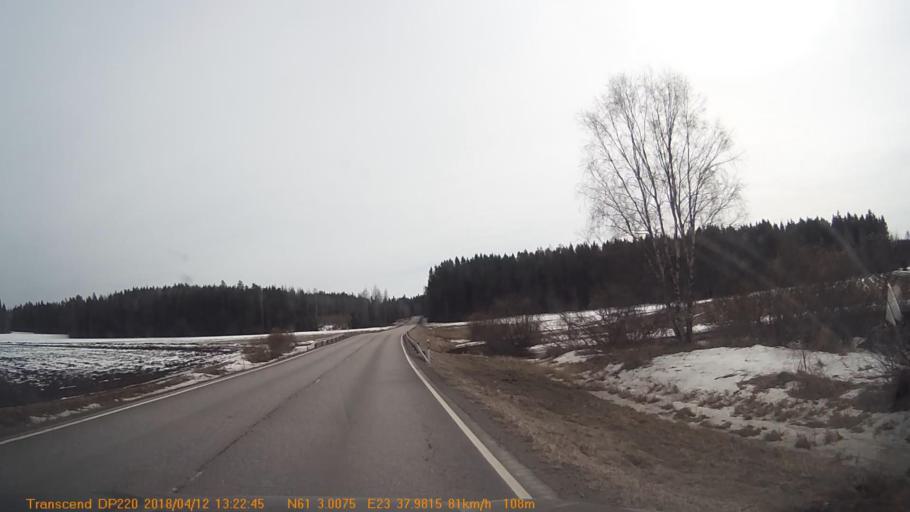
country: FI
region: Pirkanmaa
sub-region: Etelae-Pirkanmaa
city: Urjala
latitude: 61.0492
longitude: 23.6341
